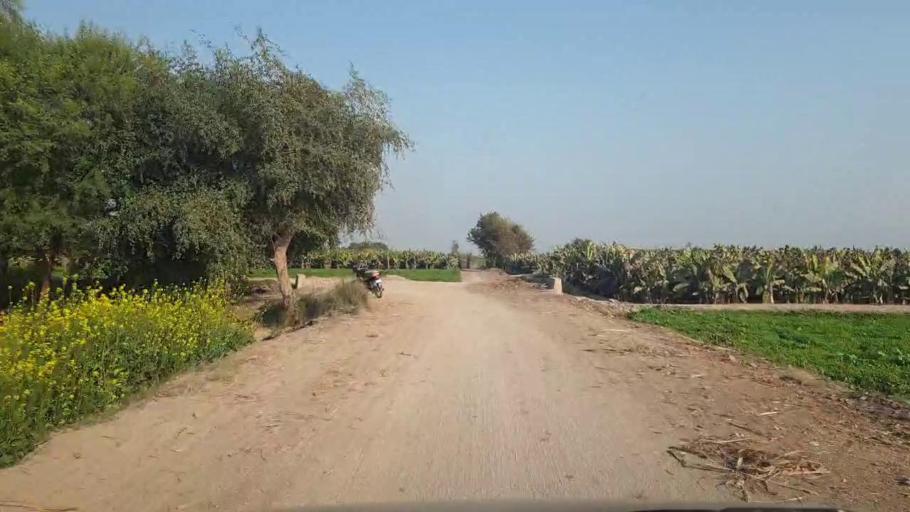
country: PK
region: Sindh
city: Bhit Shah
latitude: 25.8253
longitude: 68.5197
